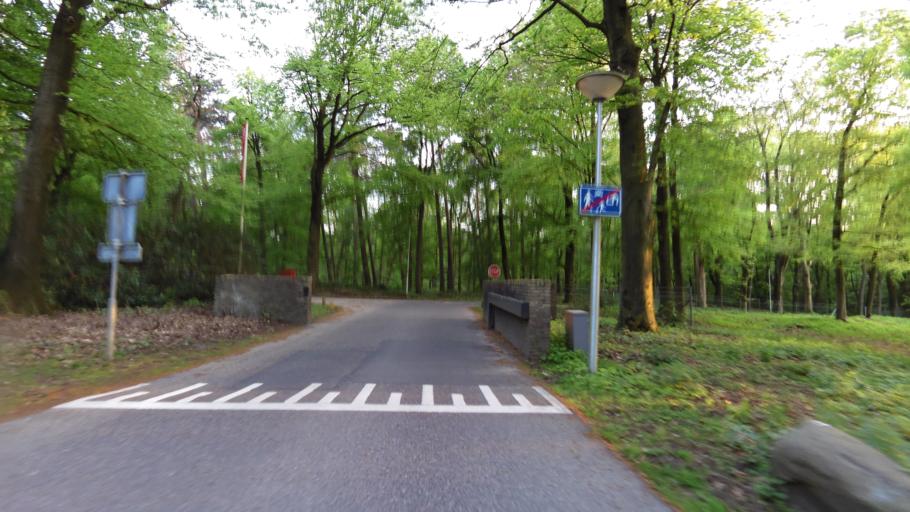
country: NL
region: Gelderland
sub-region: Gemeente Ede
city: Bennekom
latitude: 52.0200
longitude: 5.6876
